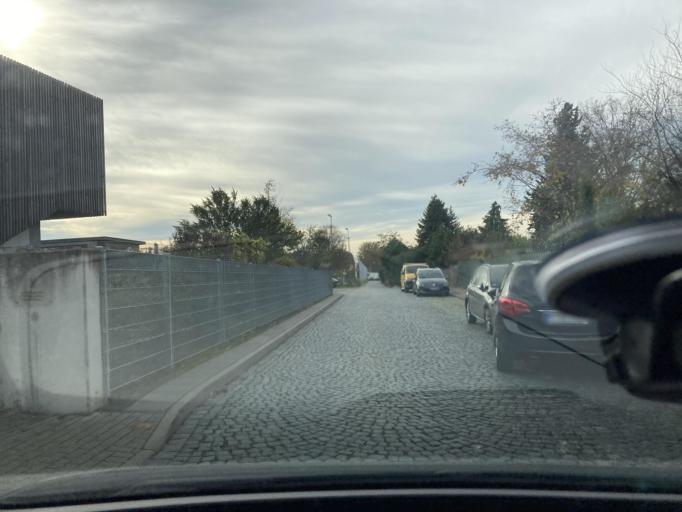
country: DE
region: Hesse
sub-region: Regierungsbezirk Darmstadt
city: Frankfurt am Main
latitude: 50.1655
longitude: 8.6790
